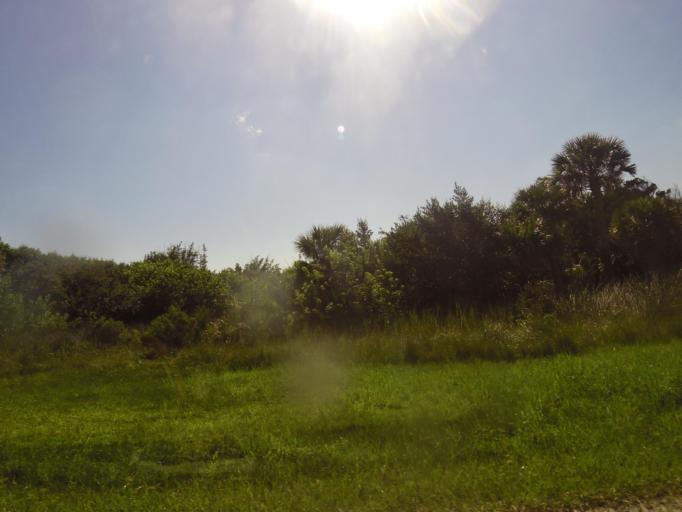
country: US
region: Florida
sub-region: Flagler County
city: Flagler Beach
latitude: 29.4449
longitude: -81.1133
